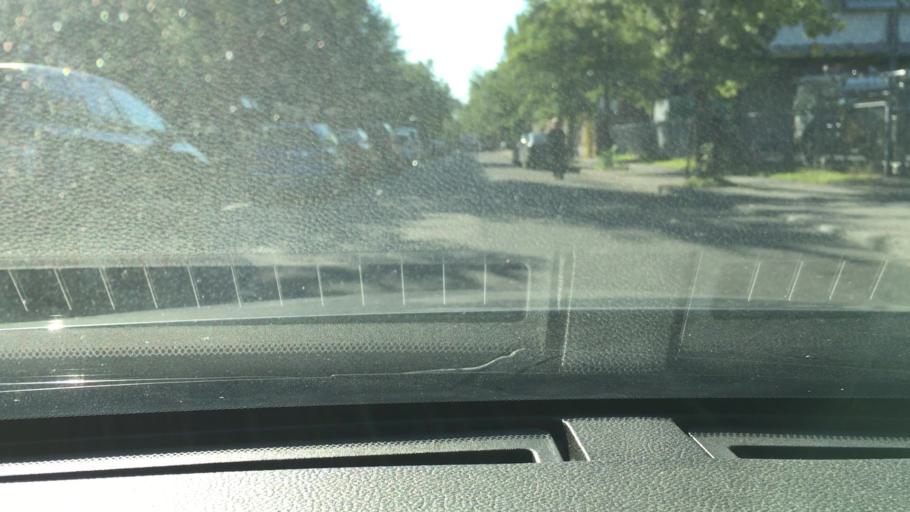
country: CA
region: Quebec
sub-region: Monteregie
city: Longueuil
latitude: 45.5521
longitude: -73.5439
